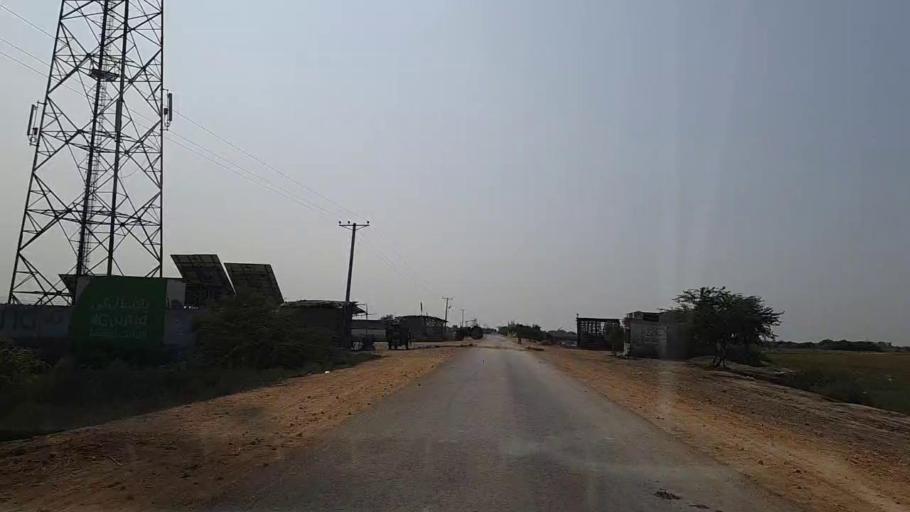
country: PK
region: Sindh
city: Chuhar Jamali
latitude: 24.2838
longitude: 67.9216
